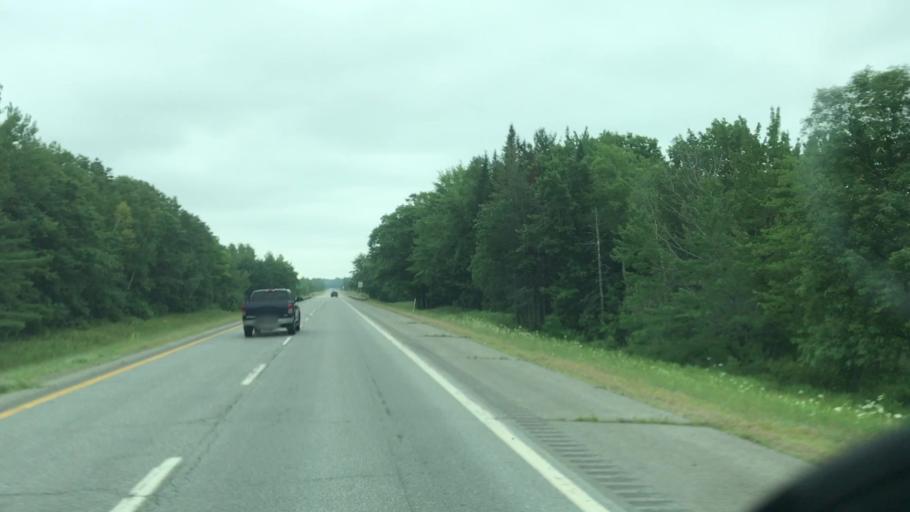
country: US
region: Maine
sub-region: Penobscot County
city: Milford
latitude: 44.9503
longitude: -68.7082
